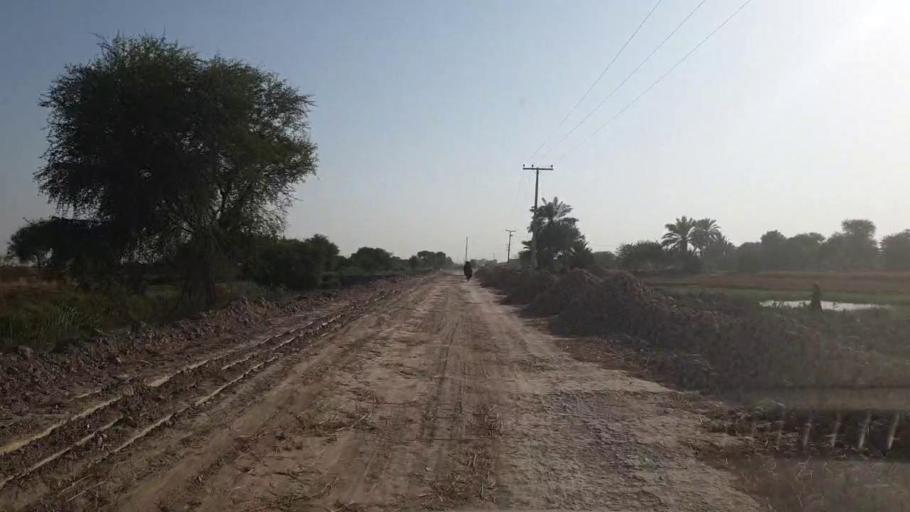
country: PK
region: Sindh
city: Talhar
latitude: 24.9230
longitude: 68.7469
